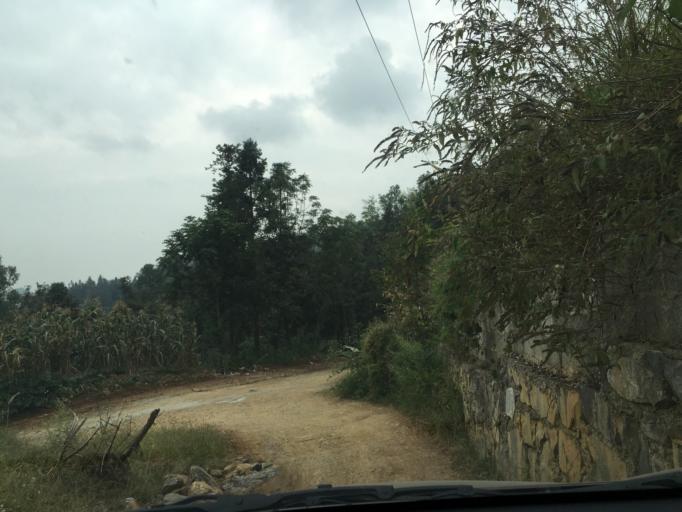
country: CN
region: Guangxi Zhuangzu Zizhiqu
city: Xinzhou
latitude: 25.5382
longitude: 105.5279
